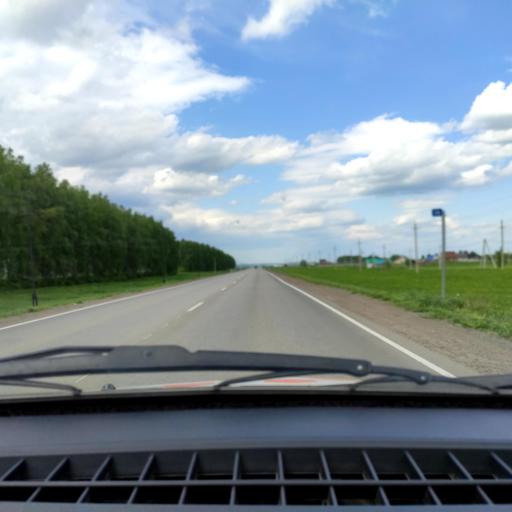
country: RU
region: Bashkortostan
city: Iglino
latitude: 54.9998
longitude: 56.4996
